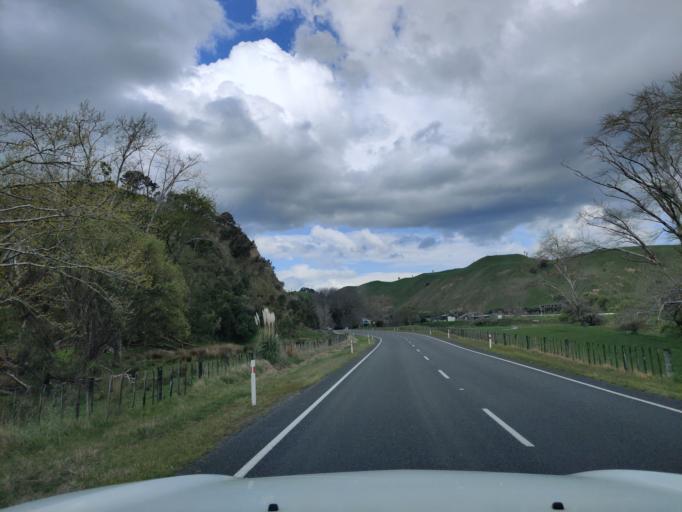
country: NZ
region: Manawatu-Wanganui
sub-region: Wanganui District
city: Wanganui
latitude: -39.8475
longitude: 175.1330
